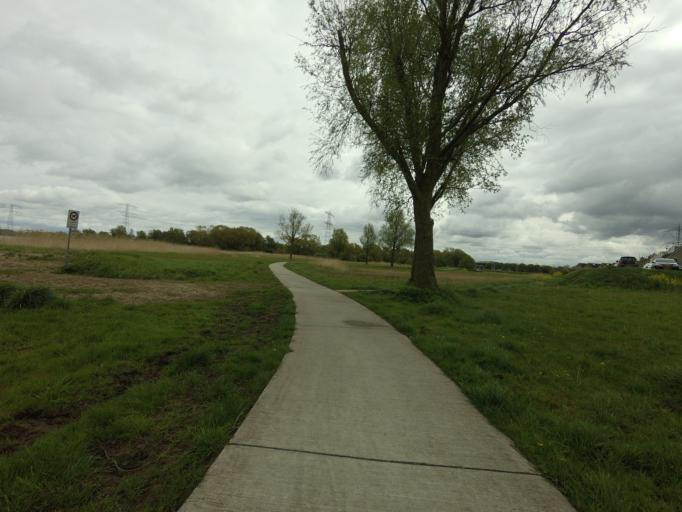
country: NL
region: North Holland
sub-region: Gemeente Naarden
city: Naarden
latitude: 52.3266
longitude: 5.1264
